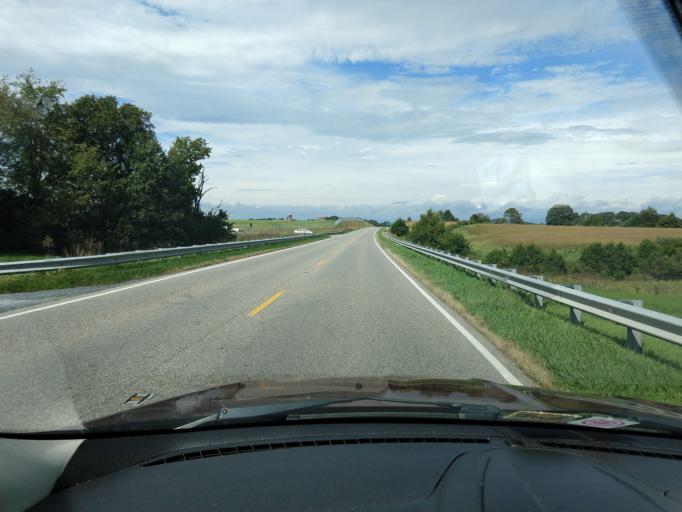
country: US
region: Virginia
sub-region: Augusta County
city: Weyers Cave
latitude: 38.2725
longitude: -78.8867
